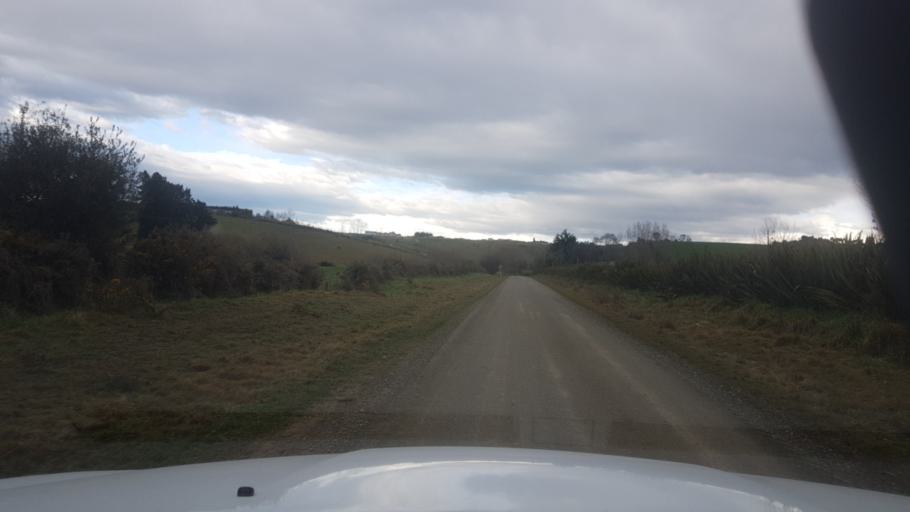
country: NZ
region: Canterbury
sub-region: Timaru District
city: Pleasant Point
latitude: -44.3427
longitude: 171.1608
